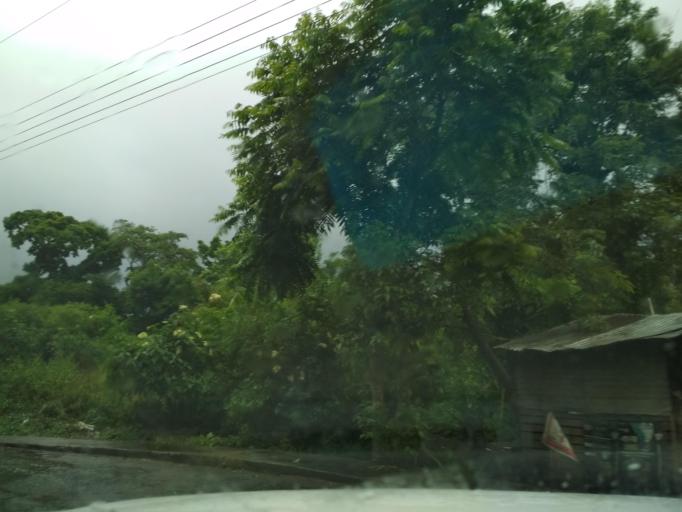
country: MX
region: Veracruz
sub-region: Mariano Escobedo
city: Chicola
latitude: 18.9020
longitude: -97.1169
